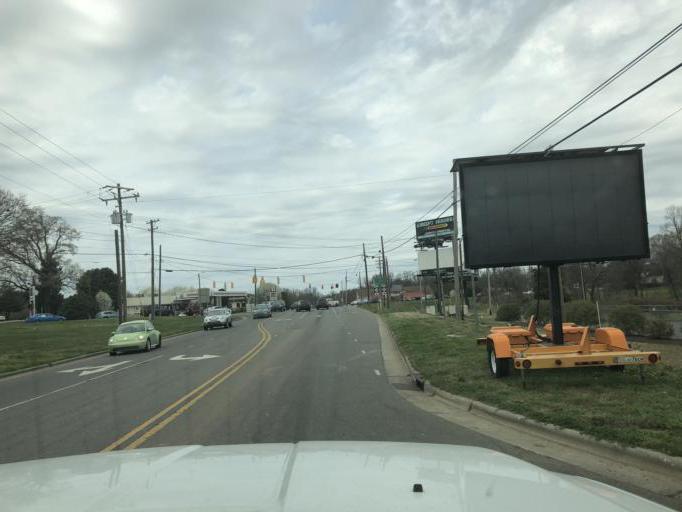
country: US
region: North Carolina
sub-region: Cleveland County
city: Shelby
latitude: 35.2827
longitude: -81.4911
